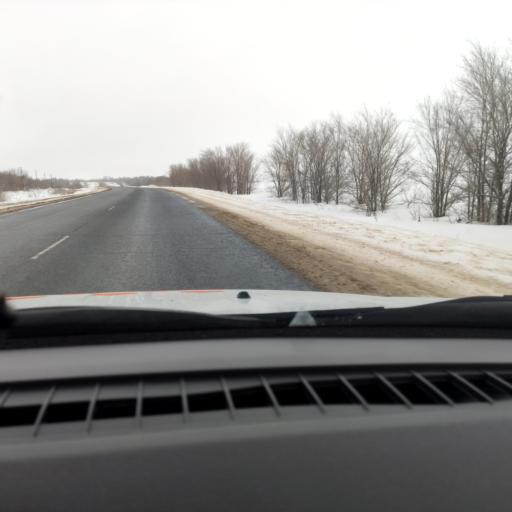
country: RU
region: Saratov
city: Perelyub
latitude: 52.3266
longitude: 50.5684
